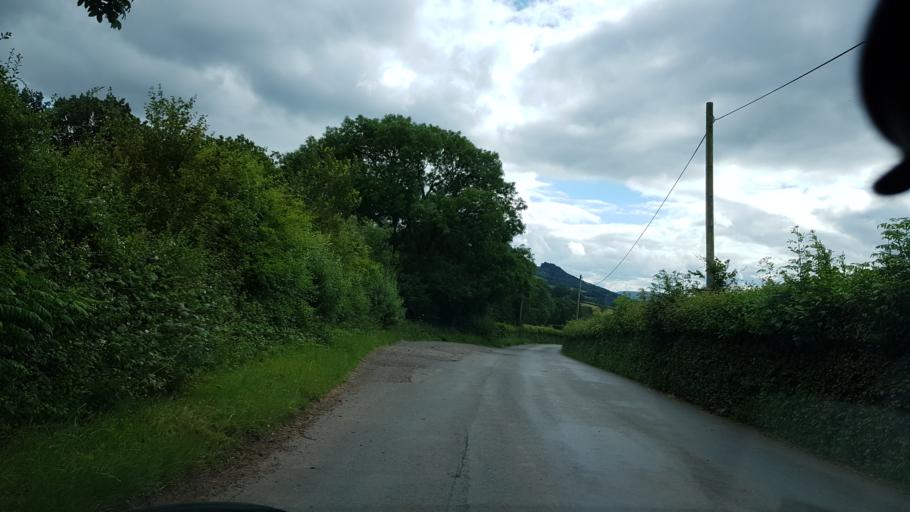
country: GB
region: England
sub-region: Herefordshire
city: Llancillo
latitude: 51.8844
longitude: -2.9530
